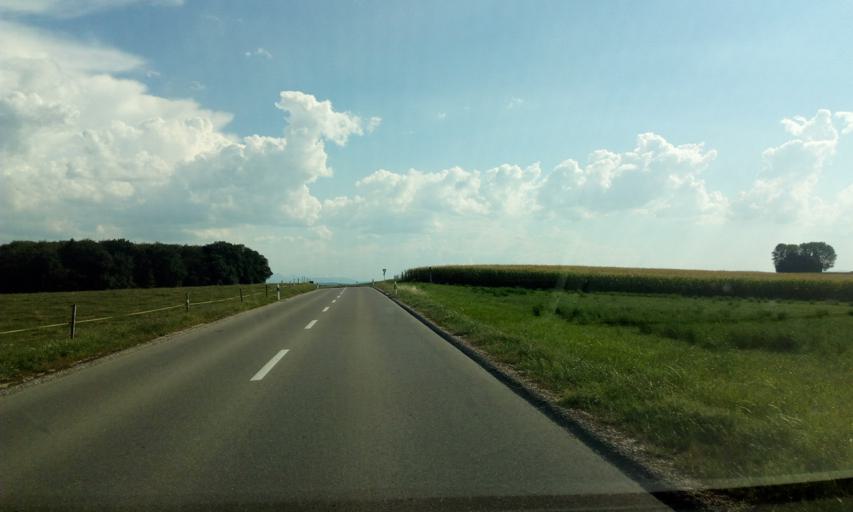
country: CH
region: Fribourg
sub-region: Broye District
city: Domdidier
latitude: 46.9086
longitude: 6.9730
